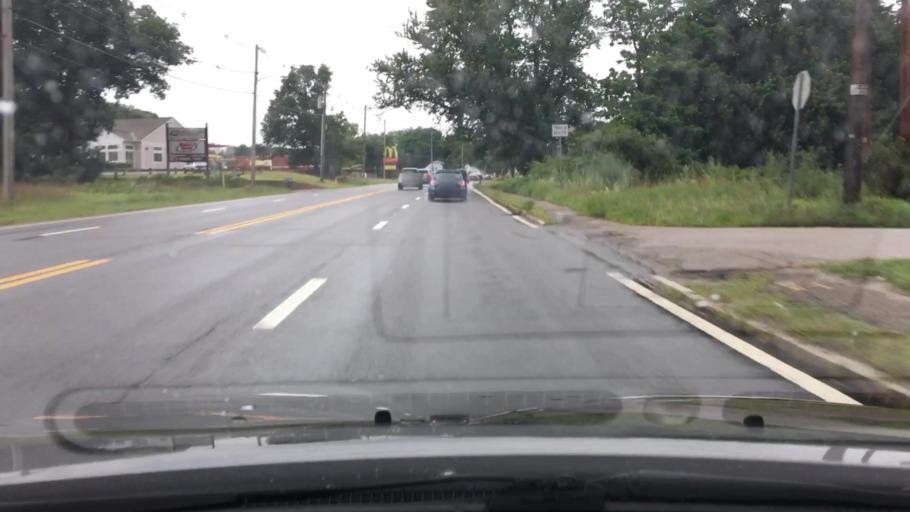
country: US
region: Rhode Island
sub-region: Providence County
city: Valley Falls
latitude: 41.9147
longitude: -71.3590
